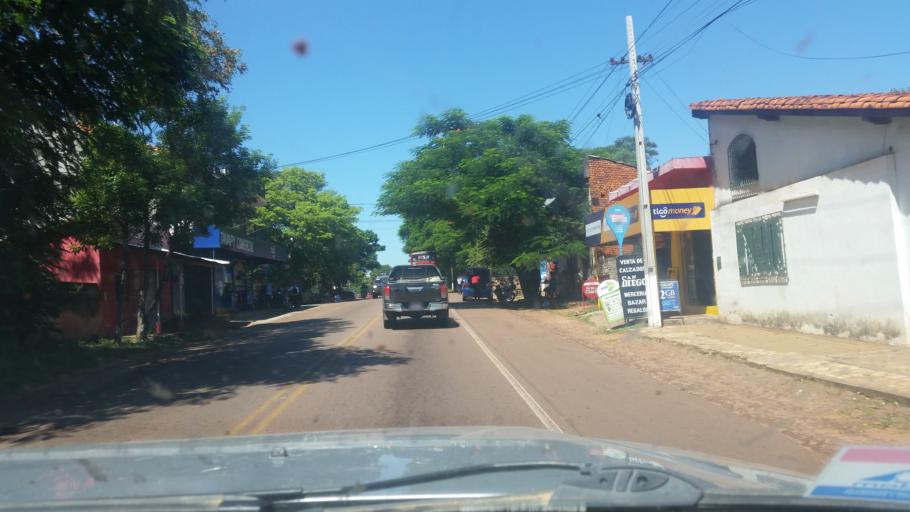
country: PY
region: Paraguari
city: Quiindy
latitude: -25.8803
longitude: -57.2900
